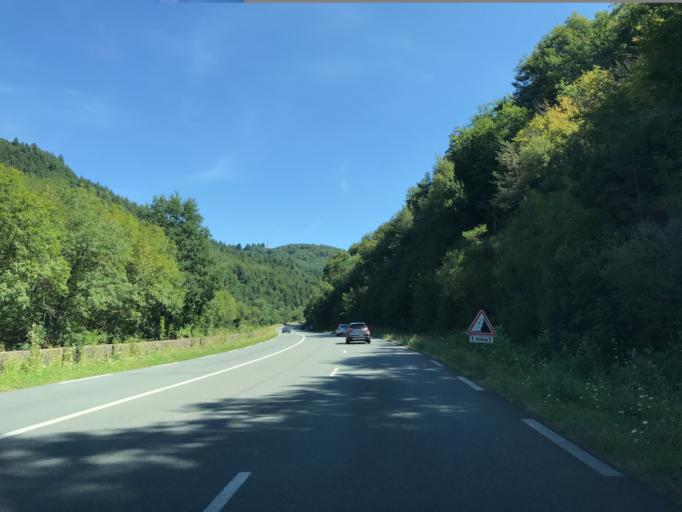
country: FR
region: Limousin
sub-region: Departement de la Correze
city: Cornil
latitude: 45.2031
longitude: 1.6626
